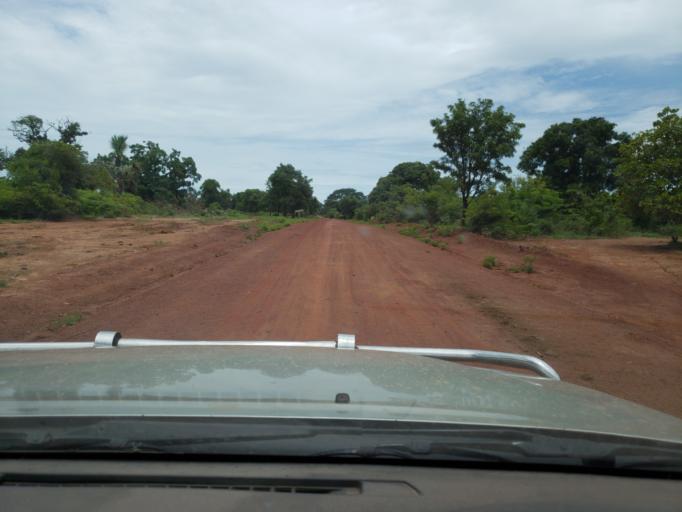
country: ML
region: Sikasso
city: Sikasso
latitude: 11.6684
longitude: -6.3421
